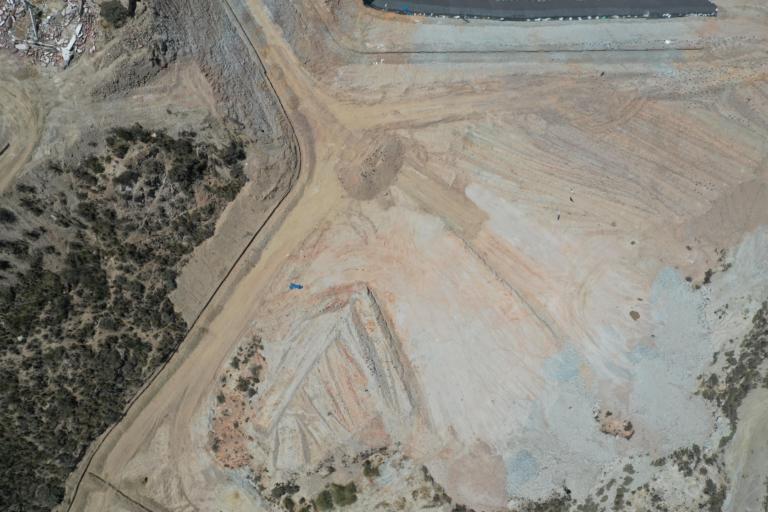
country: BO
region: La Paz
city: La Paz
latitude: -16.5552
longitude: -68.1296
